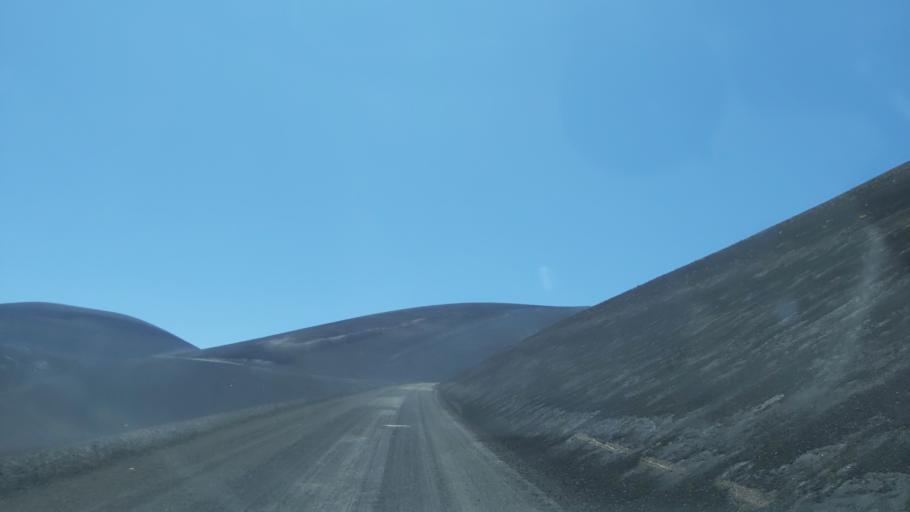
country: CL
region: Araucania
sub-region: Provincia de Cautin
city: Vilcun
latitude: -38.3943
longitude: -71.5457
